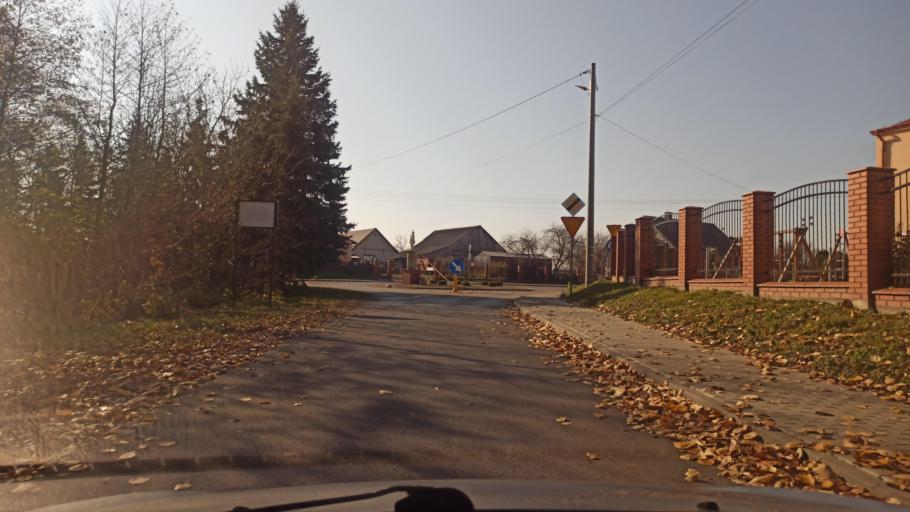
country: PL
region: Subcarpathian Voivodeship
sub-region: Powiat jaroslawski
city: Radymno
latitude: 49.9321
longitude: 22.8107
